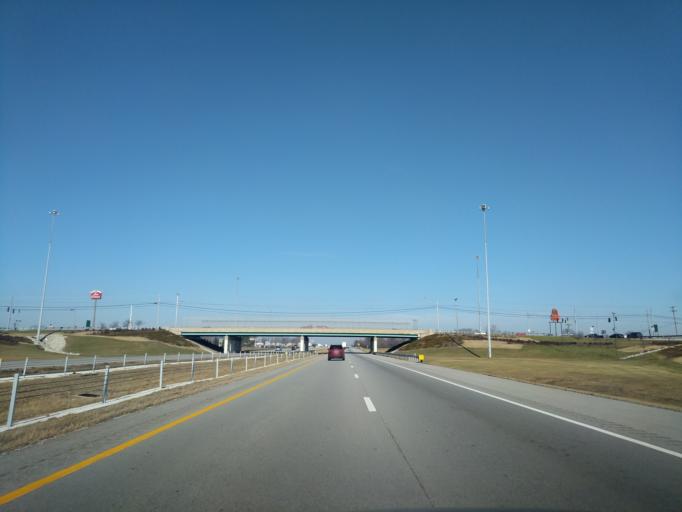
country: US
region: Ohio
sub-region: Shelby County
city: Sidney
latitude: 40.2866
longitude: -84.1823
